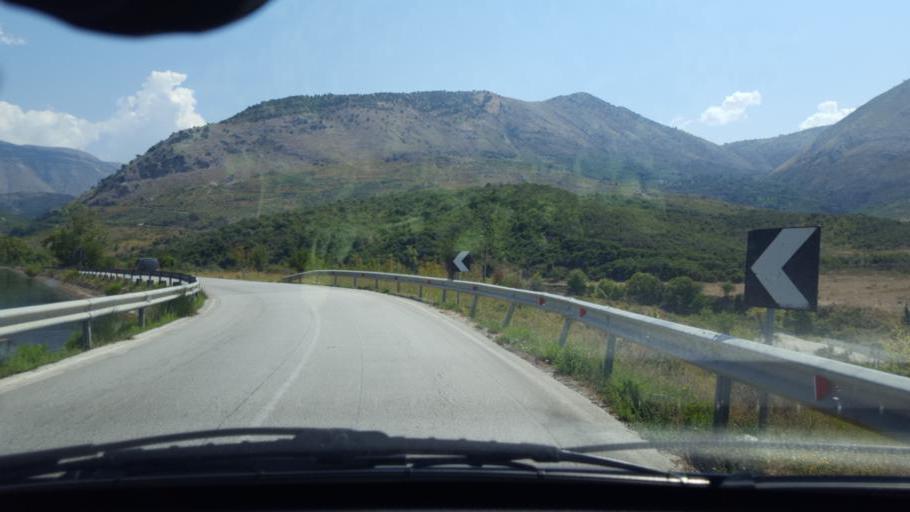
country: AL
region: Vlore
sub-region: Rrethi i Delvines
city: Mesopotam
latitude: 39.9085
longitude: 20.1242
